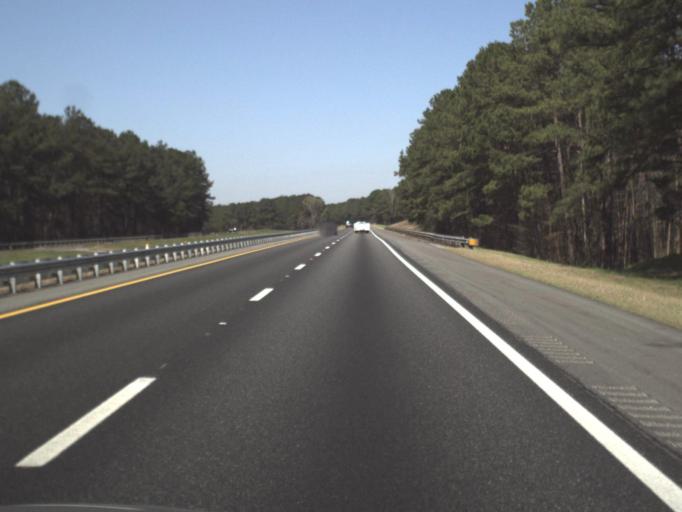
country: US
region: Florida
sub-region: Gadsden County
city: Gretna
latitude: 30.6181
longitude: -84.7690
